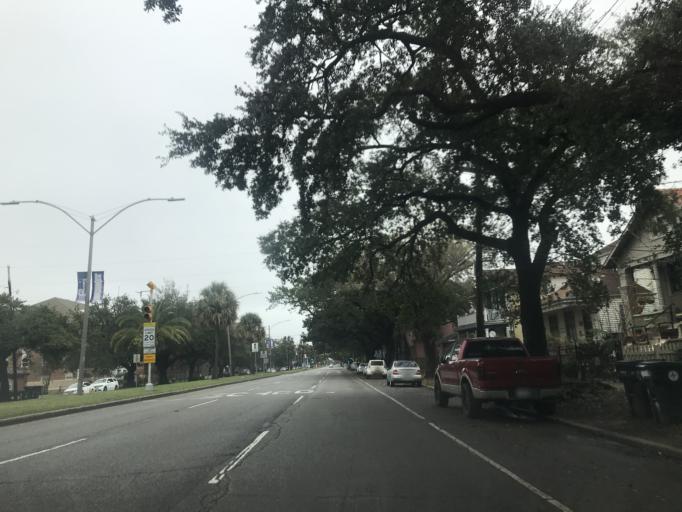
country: US
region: Louisiana
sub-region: Orleans Parish
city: New Orleans
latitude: 29.9705
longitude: -90.1047
